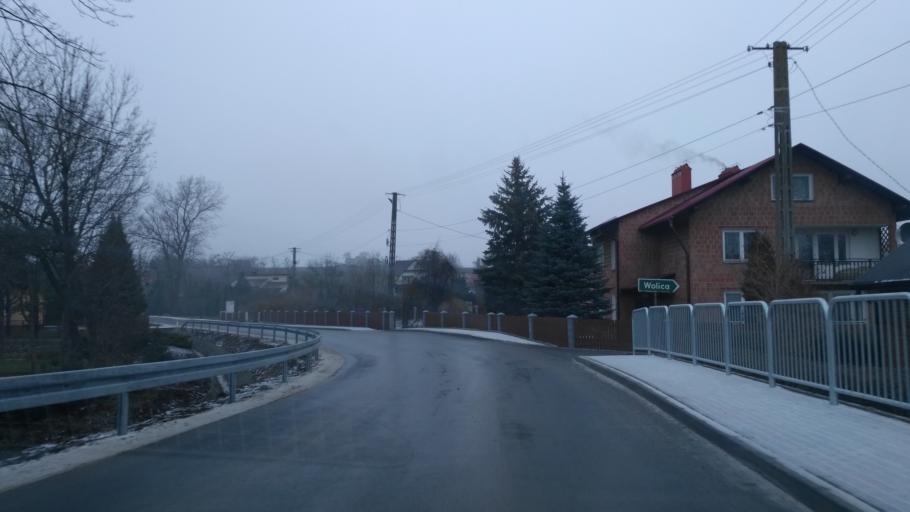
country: PL
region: Subcarpathian Voivodeship
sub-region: Powiat przeworski
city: Gac
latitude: 50.0229
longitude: 22.3936
